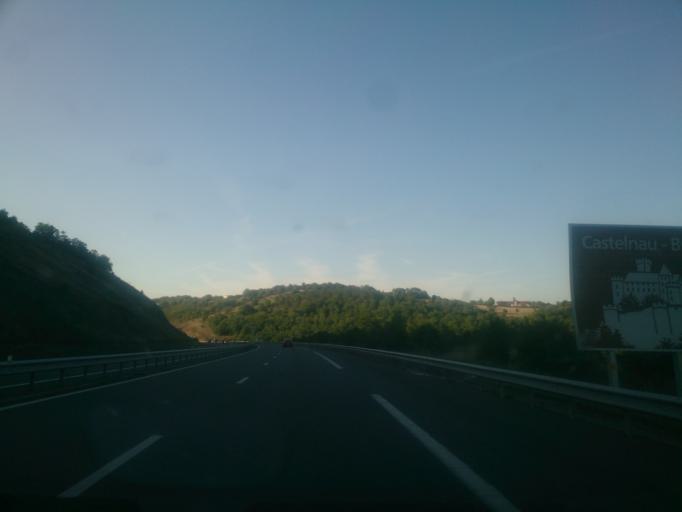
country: FR
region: Midi-Pyrenees
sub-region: Departement du Lot
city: Le Vigan
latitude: 44.7354
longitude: 1.5559
